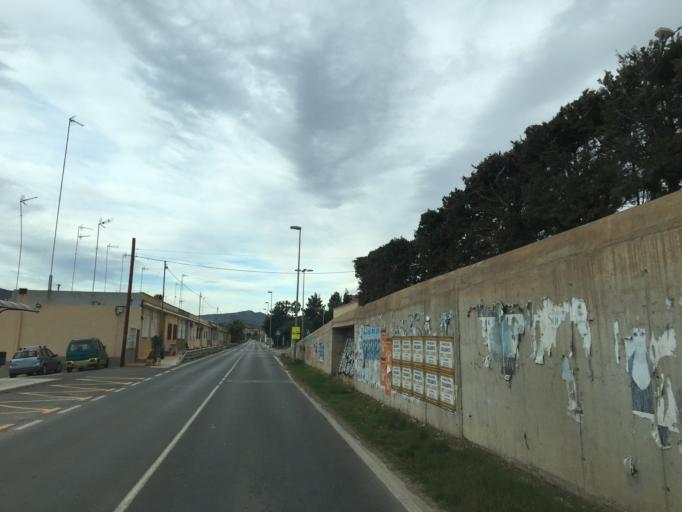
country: ES
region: Murcia
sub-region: Murcia
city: Cartagena
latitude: 37.6115
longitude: -1.0306
